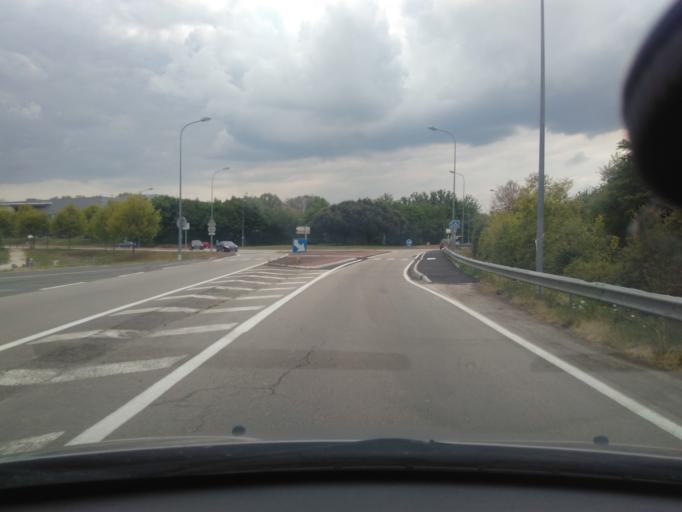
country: FR
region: Pays de la Loire
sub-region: Departement de la Vendee
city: La Roche-sur-Yon
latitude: 46.6959
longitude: -1.4243
